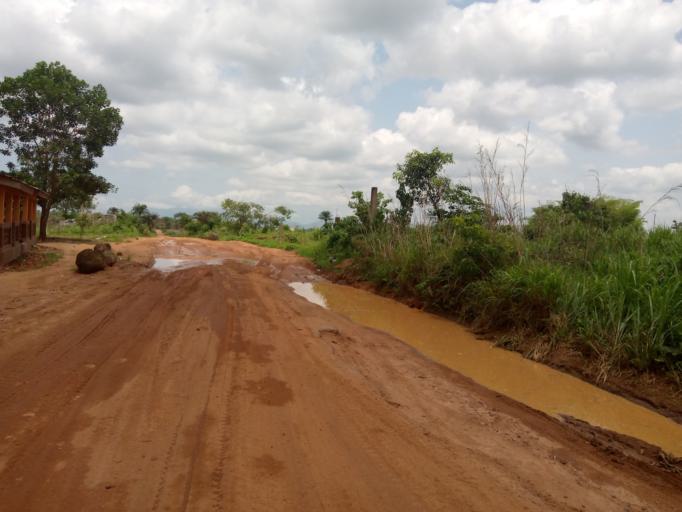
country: SL
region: Western Area
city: Waterloo
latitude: 8.3870
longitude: -12.9527
